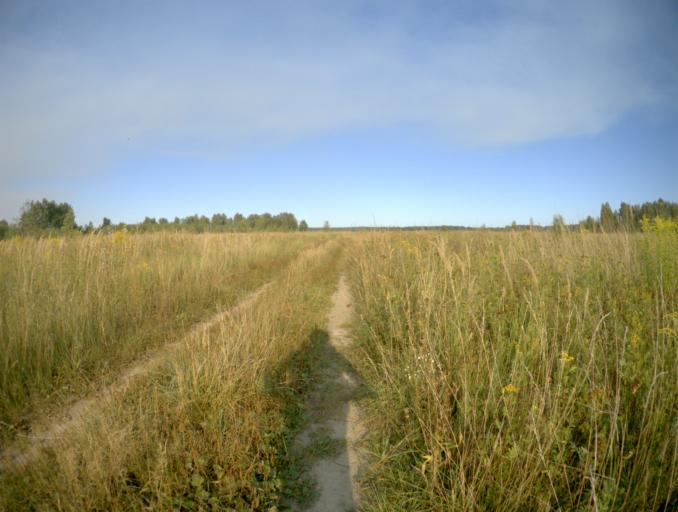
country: RU
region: Vladimir
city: Kosterevo
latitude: 55.9186
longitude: 39.7120
